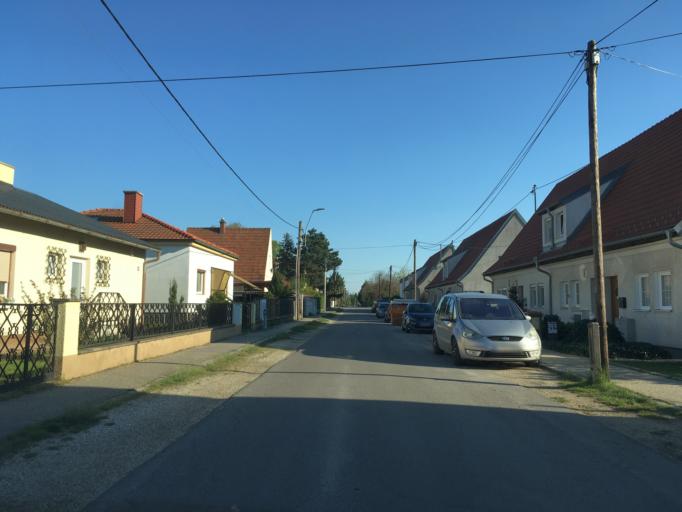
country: AT
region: Lower Austria
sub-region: Politischer Bezirk Ganserndorf
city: Strasshof an der Nordbahn
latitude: 48.3268
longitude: 16.6749
